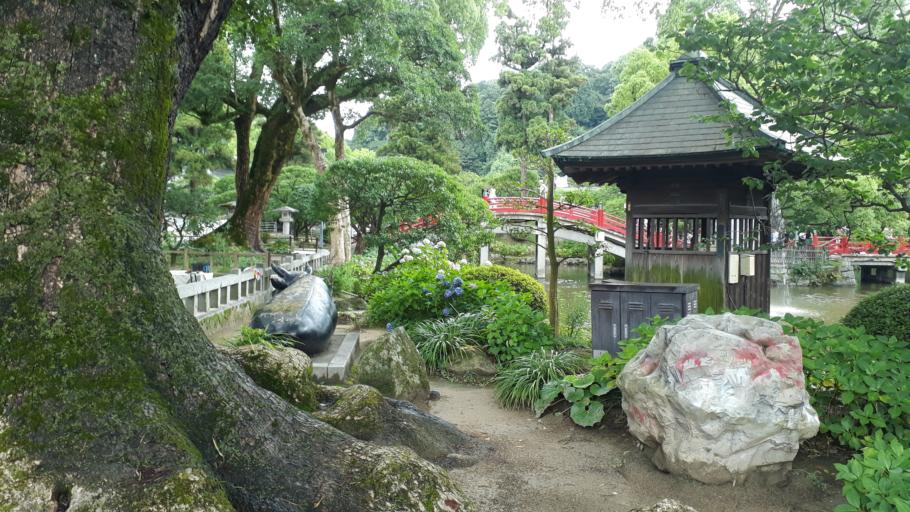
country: JP
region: Fukuoka
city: Dazaifu
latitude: 33.5203
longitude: 130.5342
